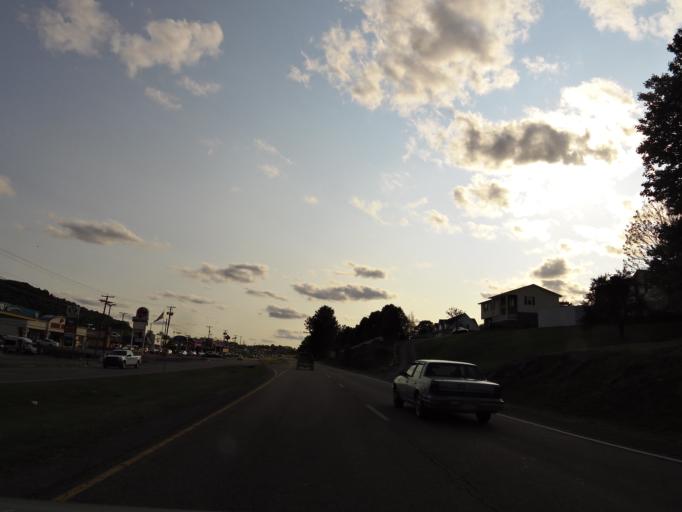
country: US
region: Virginia
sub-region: Tazewell County
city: Claypool Hill
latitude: 37.0664
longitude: -81.7364
